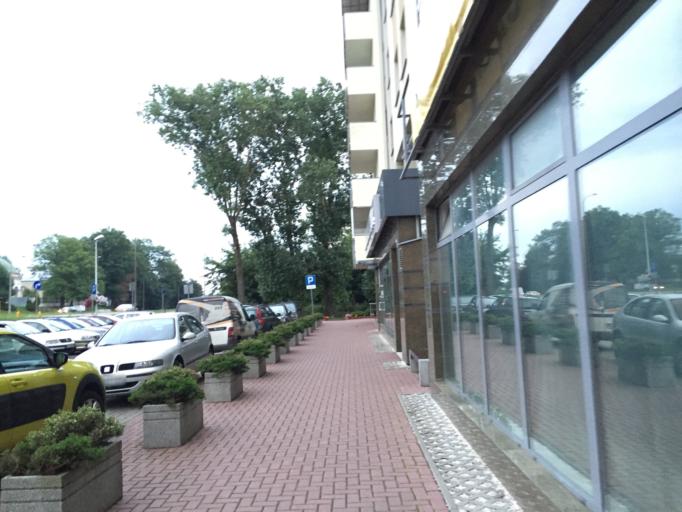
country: PL
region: Podlasie
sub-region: Bialystok
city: Bialystok
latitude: 53.1404
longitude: 23.1019
